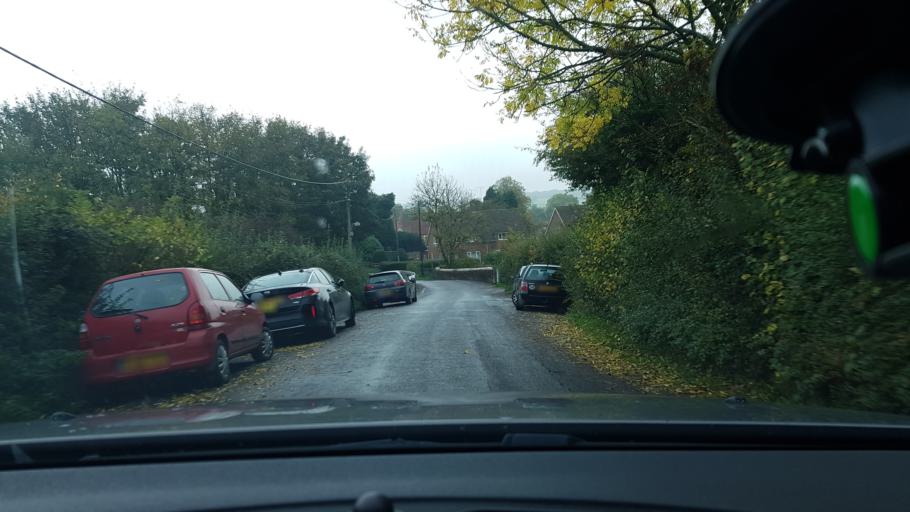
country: GB
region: England
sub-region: Wiltshire
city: Burbage
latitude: 51.3645
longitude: -1.7160
